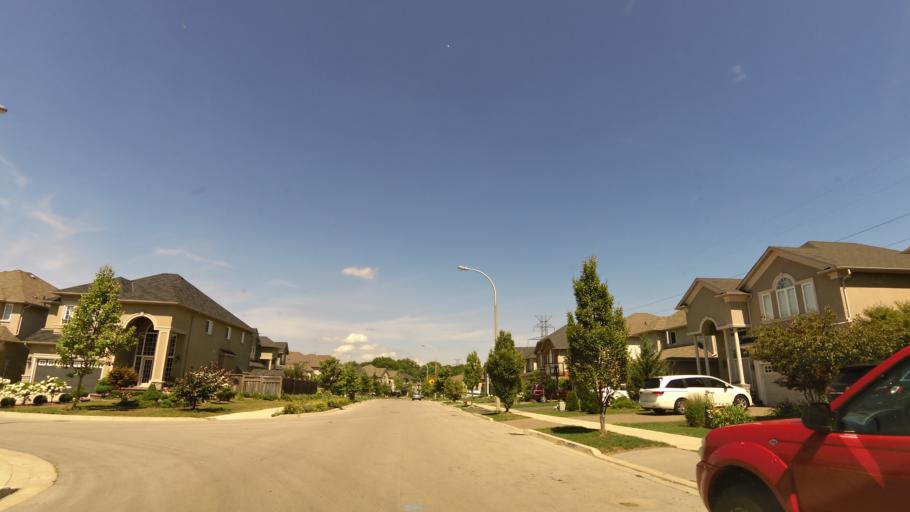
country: CA
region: Ontario
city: Ancaster
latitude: 43.2155
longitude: -79.9421
